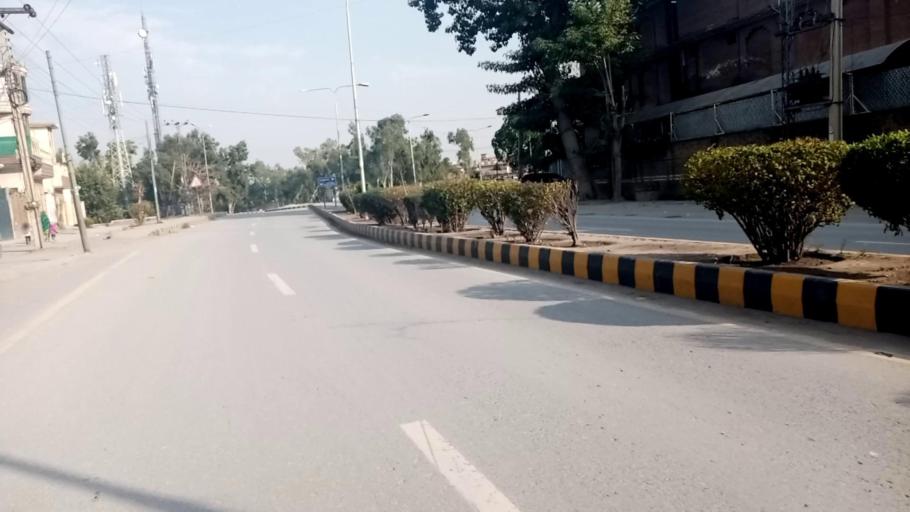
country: PK
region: Khyber Pakhtunkhwa
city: Peshawar
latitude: 33.9888
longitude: 71.4505
